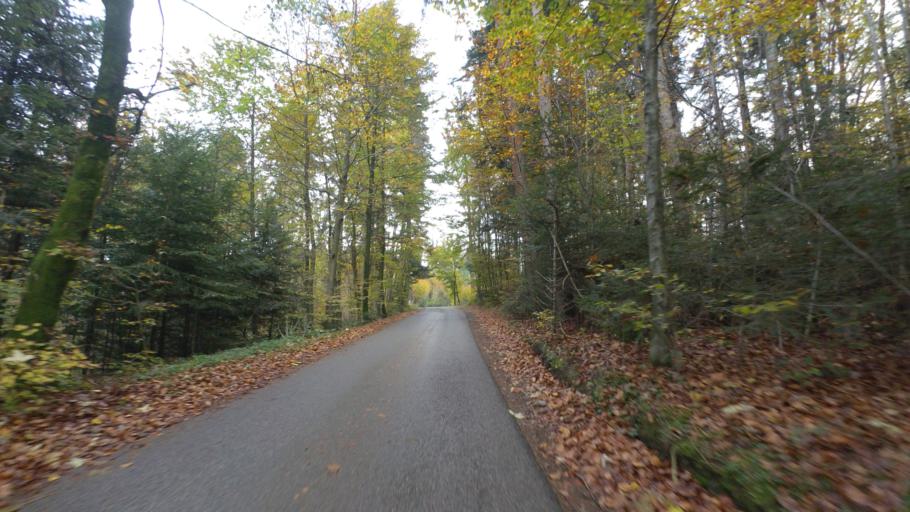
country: DE
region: Bavaria
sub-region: Upper Bavaria
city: Nussdorf
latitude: 47.9186
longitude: 12.5919
